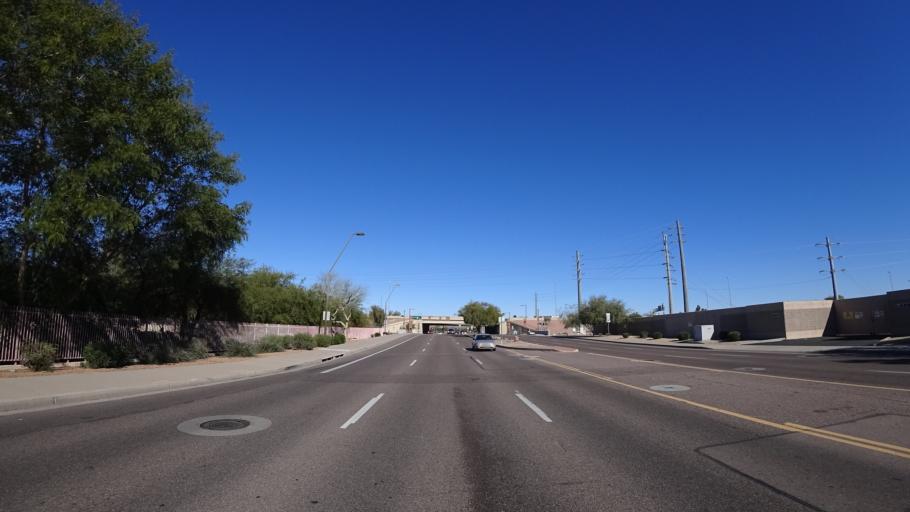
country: US
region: Arizona
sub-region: Maricopa County
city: Guadalupe
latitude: 33.3855
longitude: -111.9610
